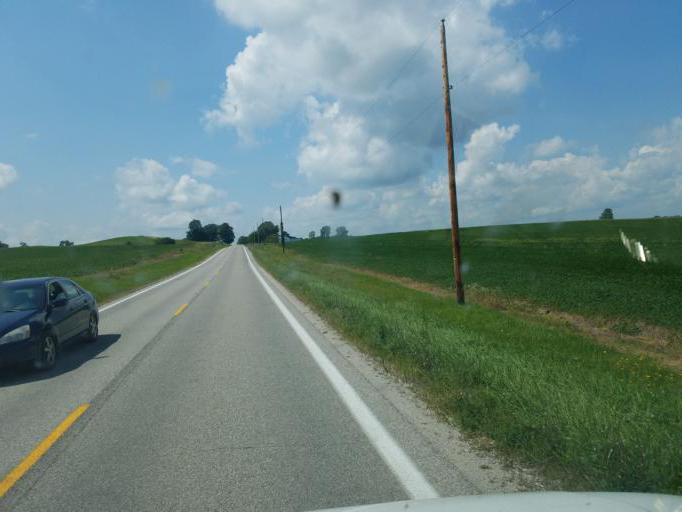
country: US
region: Ohio
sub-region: Knox County
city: Centerburg
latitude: 40.3921
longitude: -82.7052
